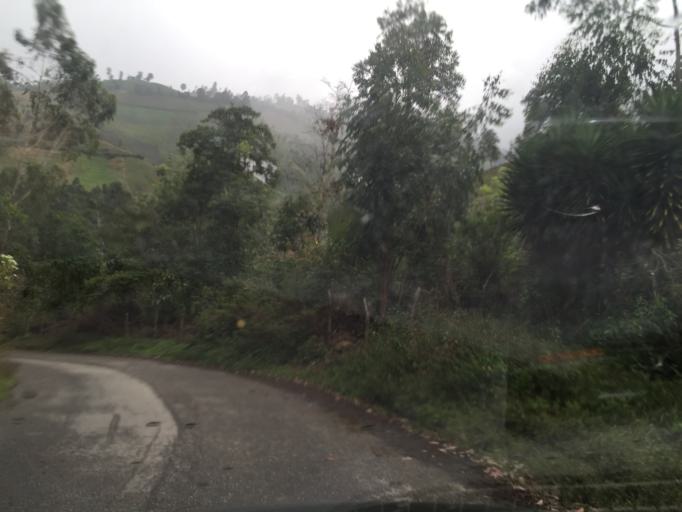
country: CO
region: Tolima
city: Cajamarca
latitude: 4.3940
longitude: -75.4505
